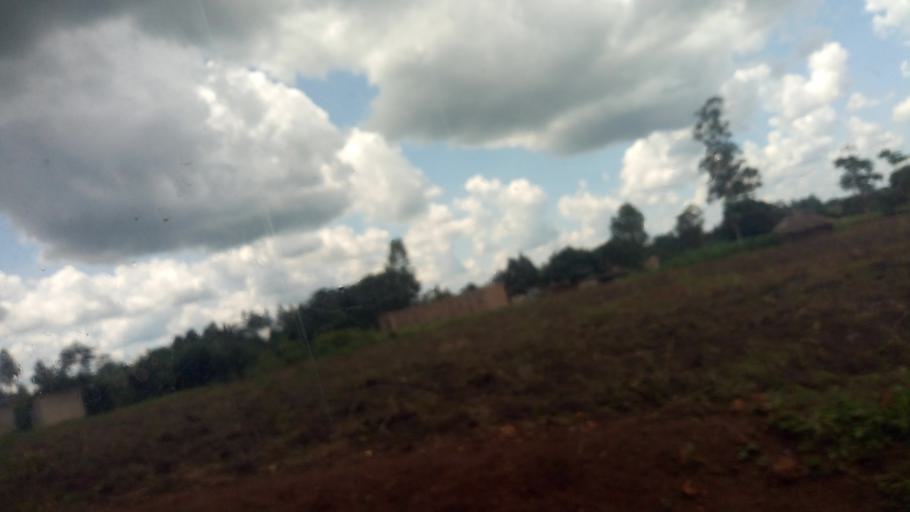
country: UG
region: Western Region
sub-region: Kiryandongo District
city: Kiryandongo
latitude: 1.9335
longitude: 32.1311
